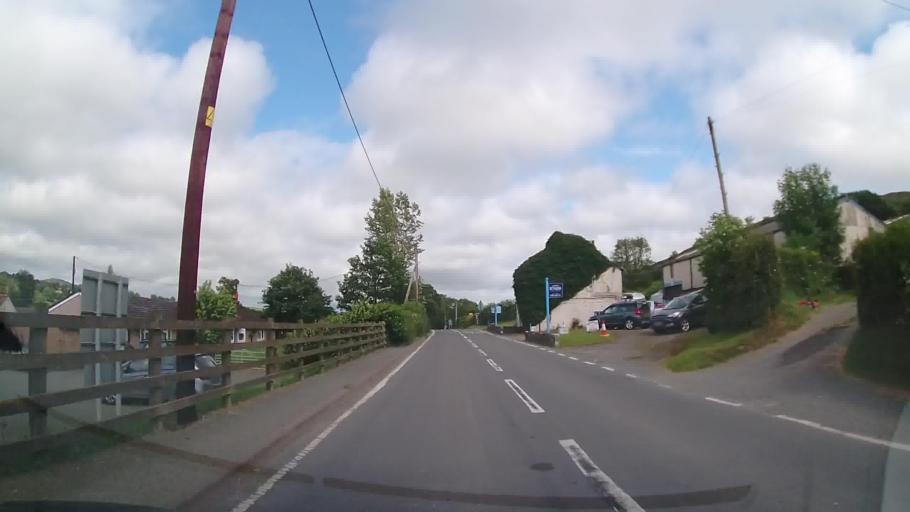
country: GB
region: Wales
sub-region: Sir Powys
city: Llangynog
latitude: 52.8107
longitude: -3.3539
